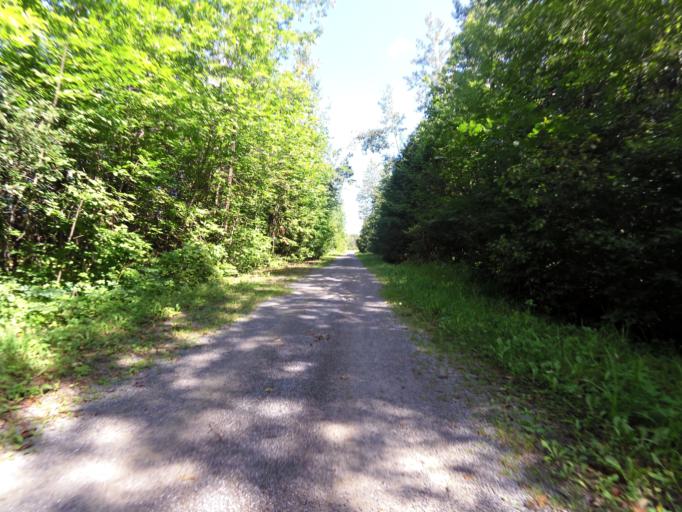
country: CA
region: Ontario
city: Ottawa
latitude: 45.2276
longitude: -75.6199
